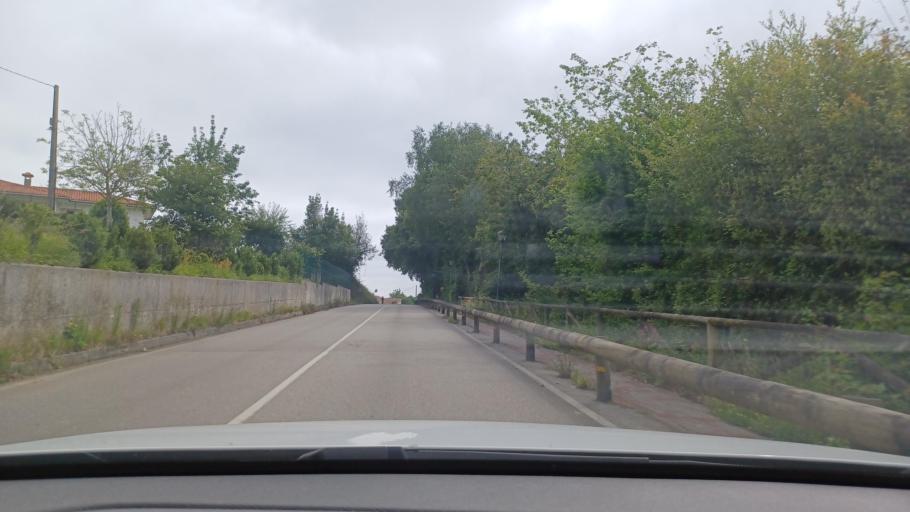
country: ES
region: Asturias
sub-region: Province of Asturias
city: Ribadesella
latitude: 43.4620
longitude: -5.0889
